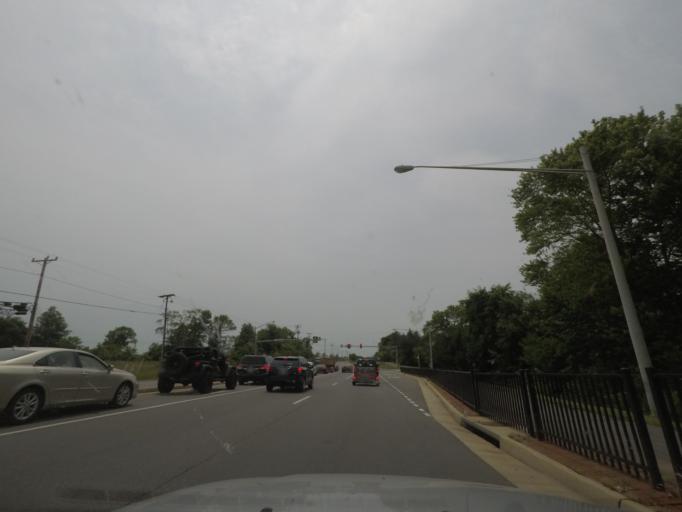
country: US
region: Virginia
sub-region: Loudoun County
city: Leesburg
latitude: 39.1001
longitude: -77.5764
